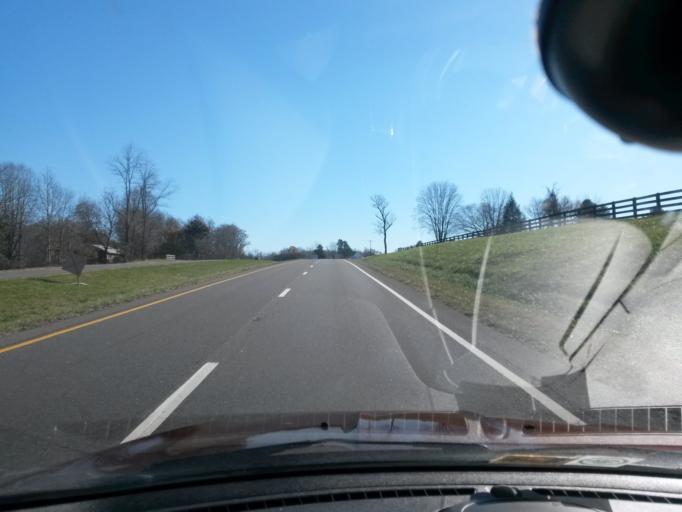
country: US
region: Virginia
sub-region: Bedford County
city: Forest
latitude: 37.3040
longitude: -79.3870
